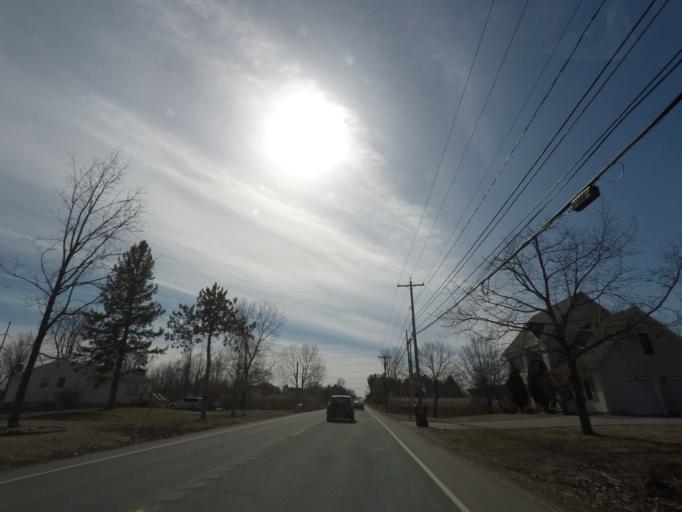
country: US
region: New York
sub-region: Albany County
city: Cohoes
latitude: 42.7661
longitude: -73.7425
